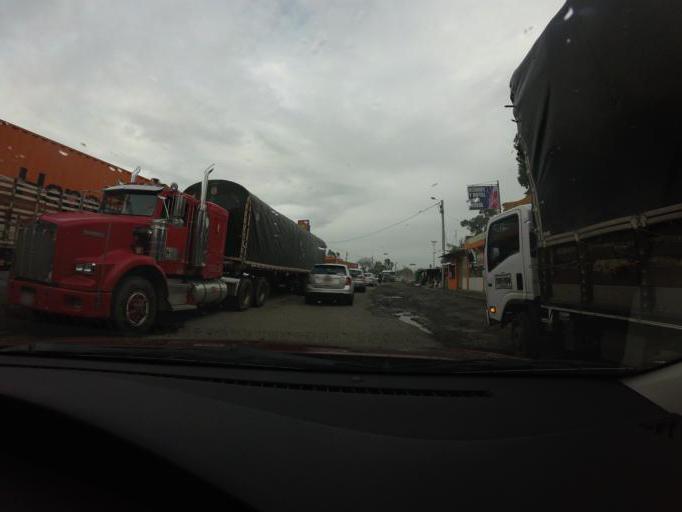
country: CO
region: Cundinamarca
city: Villeta
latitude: 5.0014
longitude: -74.5383
